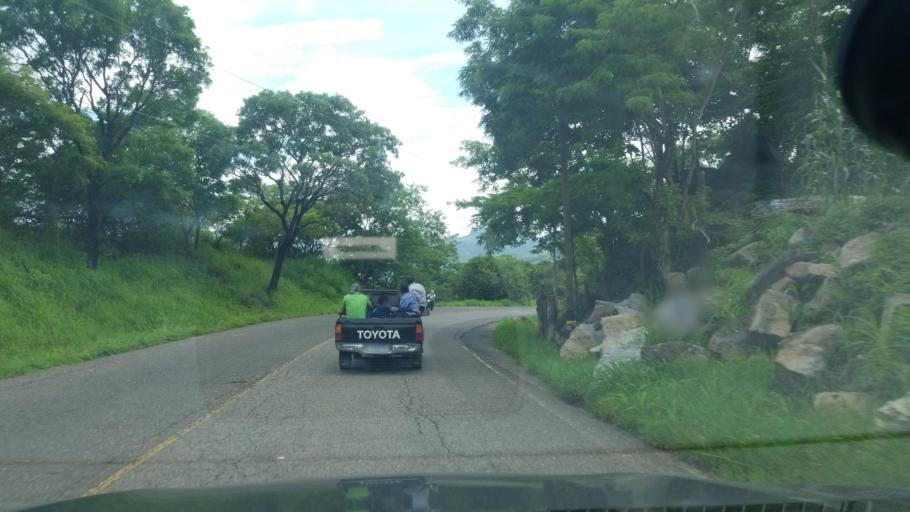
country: HN
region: Choluteca
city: Corpus
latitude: 13.3724
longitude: -87.0576
